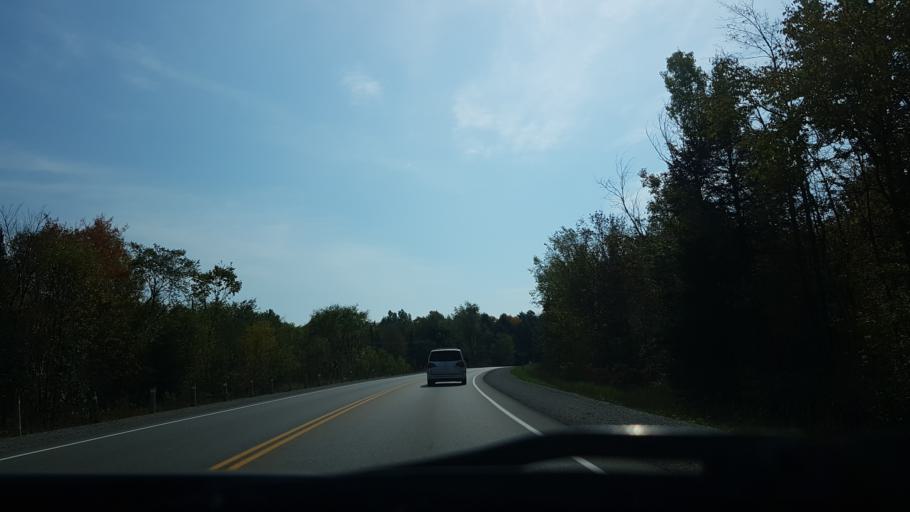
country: CA
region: Ontario
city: Orillia
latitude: 44.7391
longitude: -79.2933
